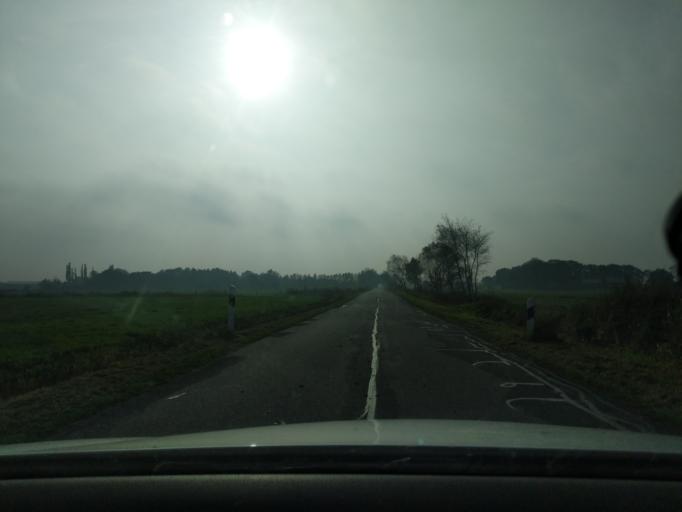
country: DE
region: Lower Saxony
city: Wanna
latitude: 53.7699
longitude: 8.7372
